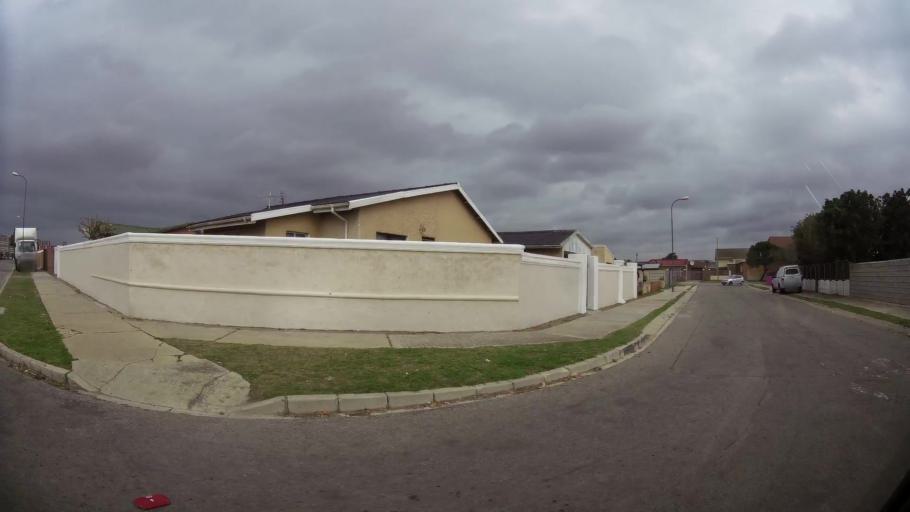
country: ZA
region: Eastern Cape
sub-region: Nelson Mandela Bay Metropolitan Municipality
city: Port Elizabeth
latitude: -33.8959
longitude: 25.5660
